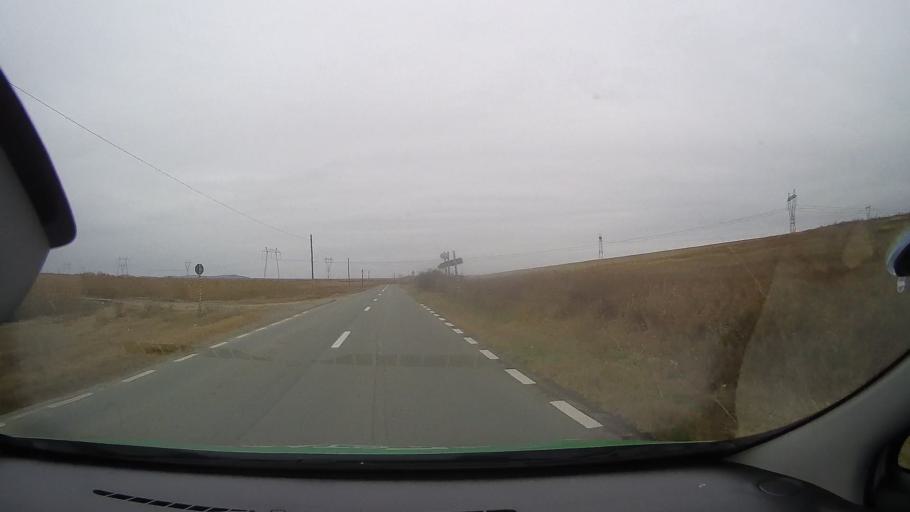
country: RO
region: Constanta
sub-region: Comuna Silistea
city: Silistea
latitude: 44.4329
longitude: 28.2190
